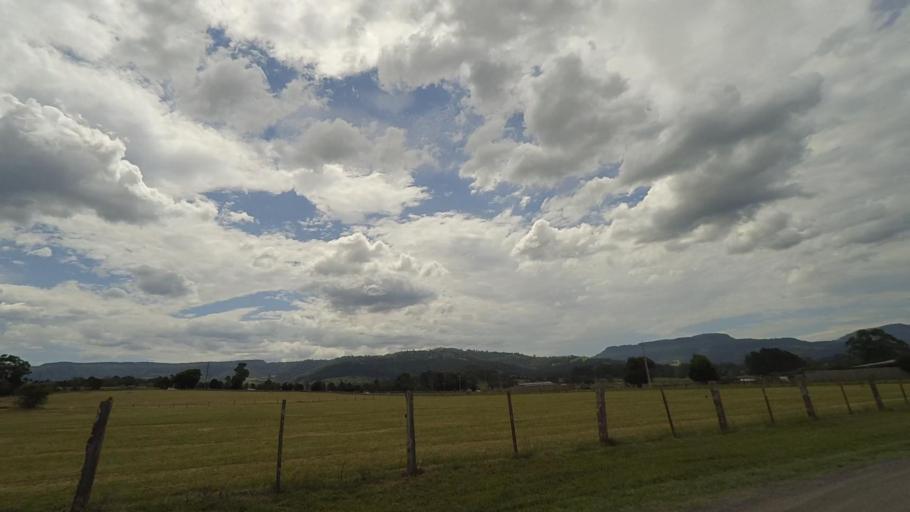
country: AU
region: New South Wales
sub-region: Shoalhaven Shire
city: Berry
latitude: -34.7934
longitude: 150.6743
